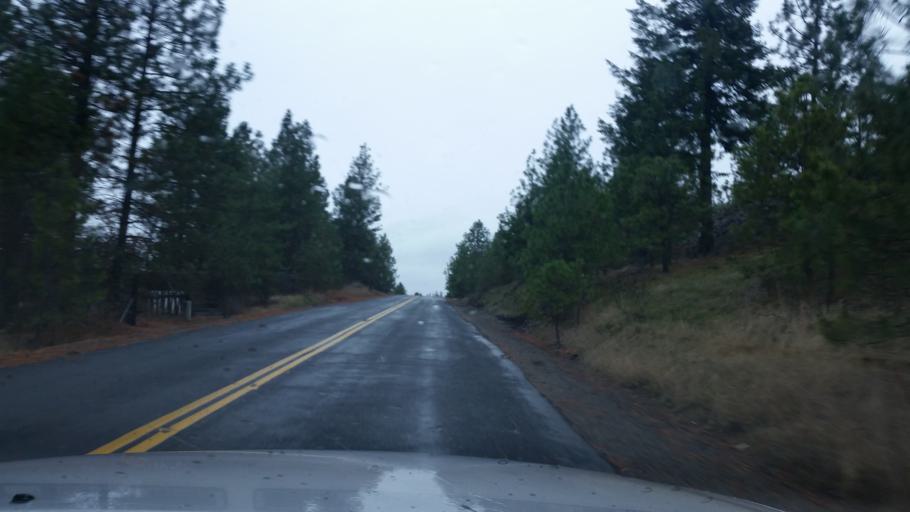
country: US
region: Washington
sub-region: Spokane County
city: Airway Heights
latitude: 47.6985
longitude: -117.5732
